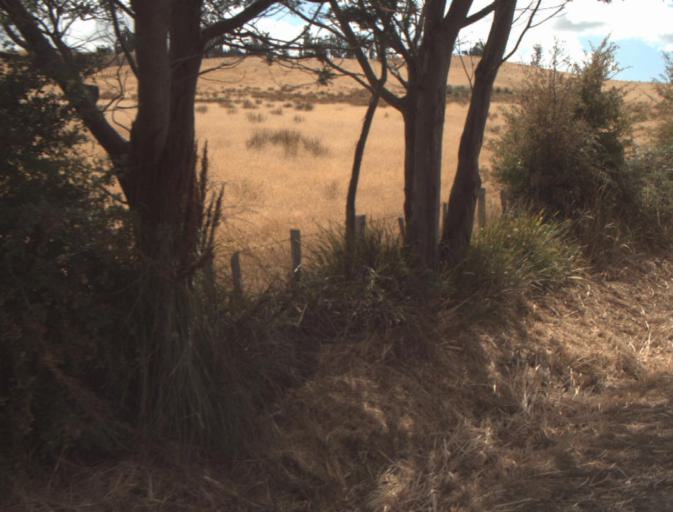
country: AU
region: Tasmania
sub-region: Launceston
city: Mayfield
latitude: -41.2221
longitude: 147.1216
